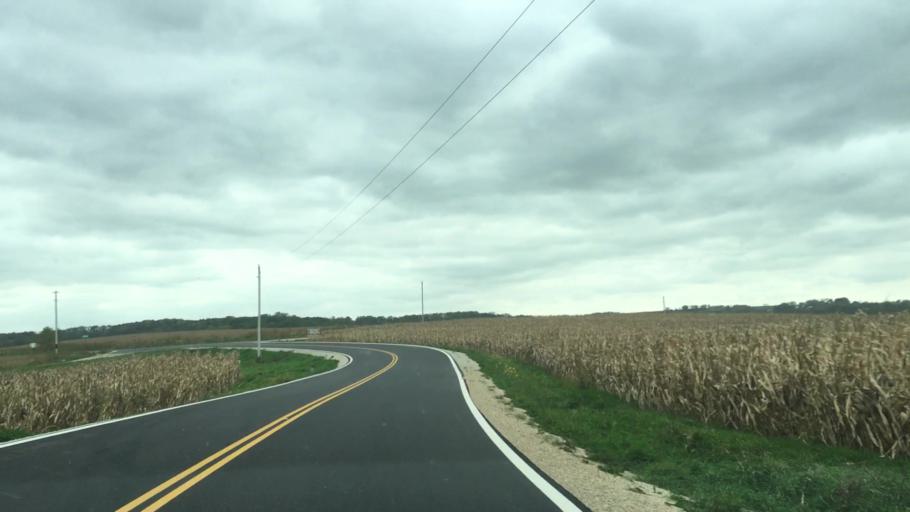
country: US
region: Minnesota
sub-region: Fillmore County
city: Preston
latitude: 43.7542
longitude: -92.0205
